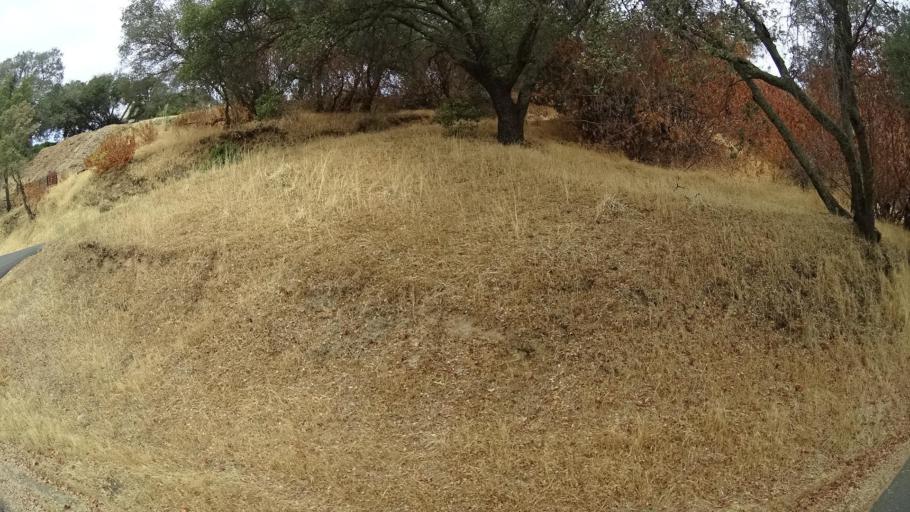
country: US
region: California
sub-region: Placer County
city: Loomis
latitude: 38.8306
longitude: -121.2209
